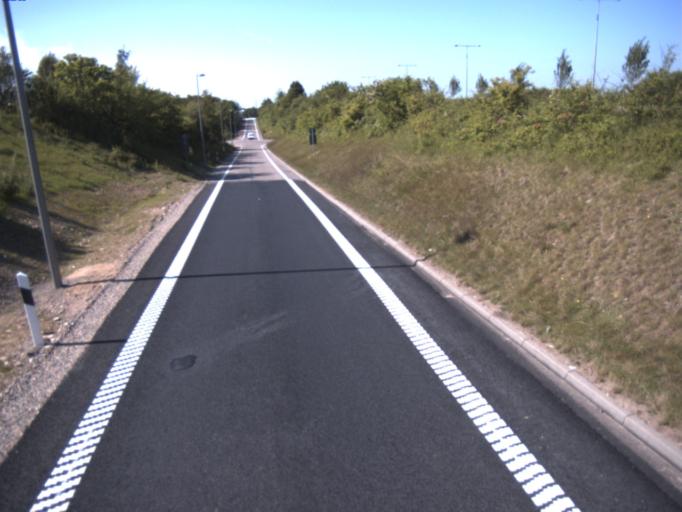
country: SE
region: Skane
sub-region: Helsingborg
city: Odakra
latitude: 56.0726
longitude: 12.7398
